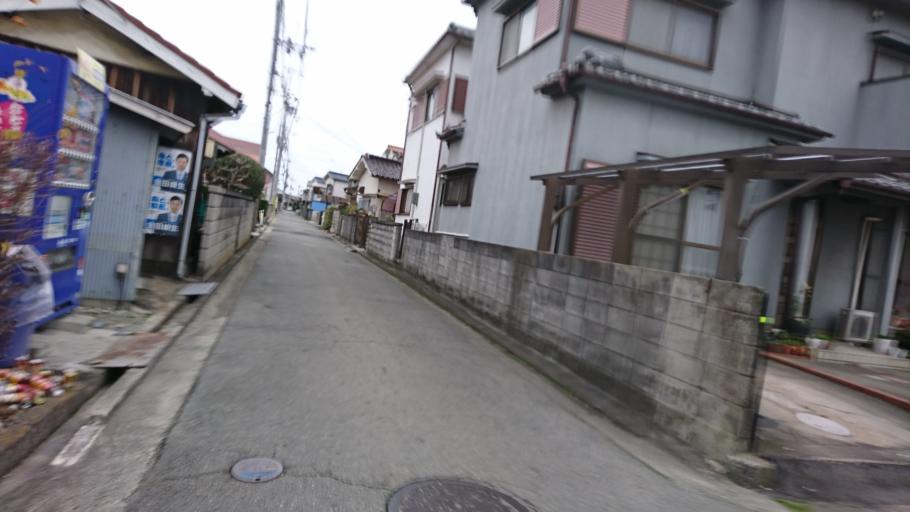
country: JP
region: Hyogo
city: Kakogawacho-honmachi
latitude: 34.7466
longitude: 134.8571
